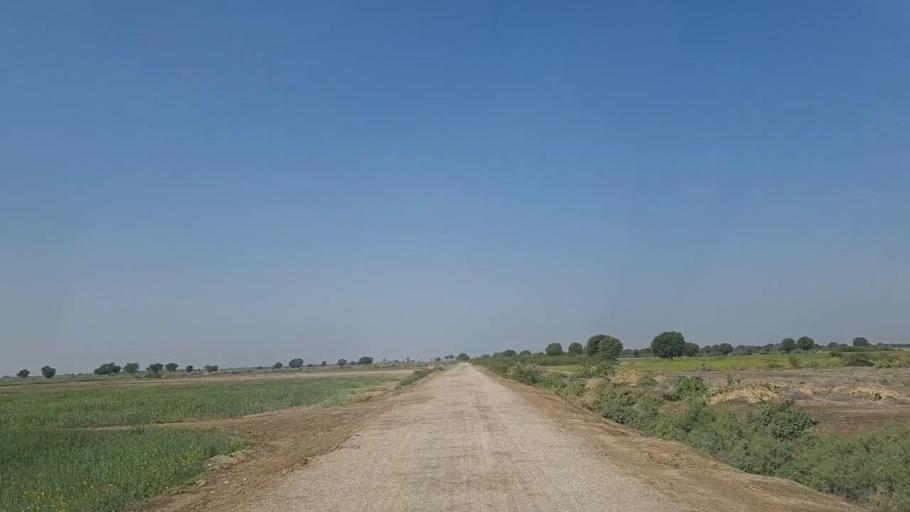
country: PK
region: Sindh
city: Digri
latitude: 25.1941
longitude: 69.1414
